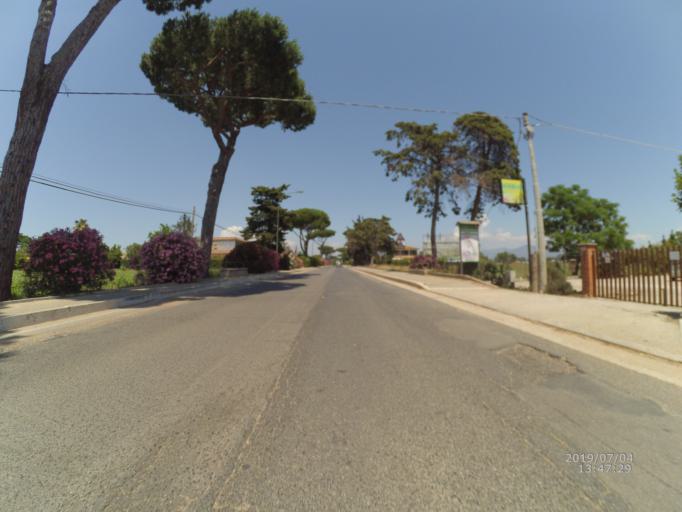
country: IT
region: Latium
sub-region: Provincia di Latina
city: San Felice Circeo
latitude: 41.2779
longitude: 13.1016
